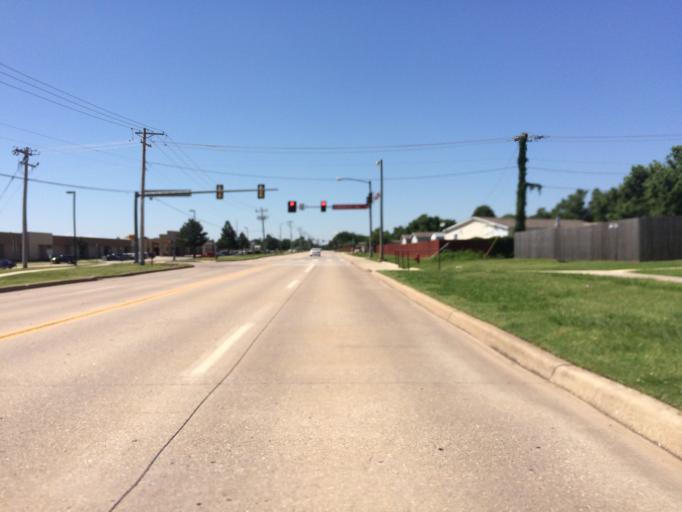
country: US
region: Oklahoma
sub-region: Cleveland County
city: Norman
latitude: 35.2424
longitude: -97.4501
